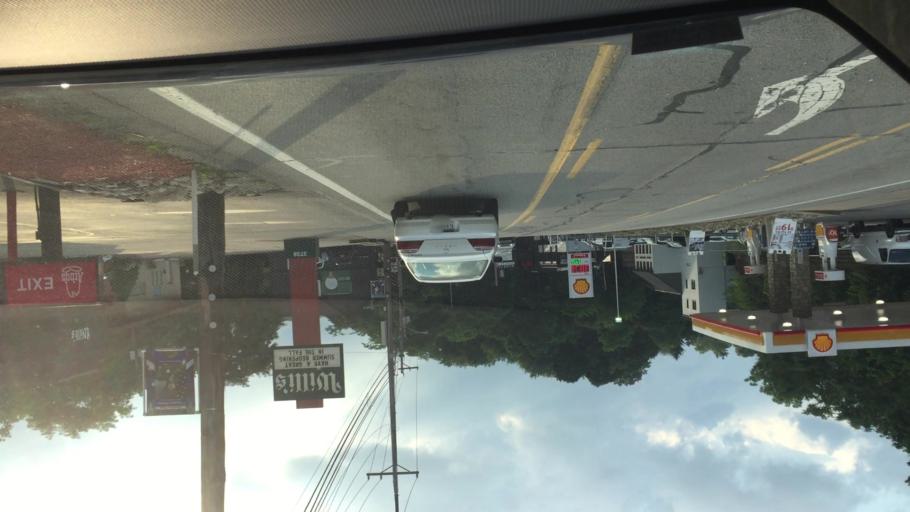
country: US
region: Pennsylvania
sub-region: Allegheny County
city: Castle Shannon
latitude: 40.3647
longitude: -80.0204
